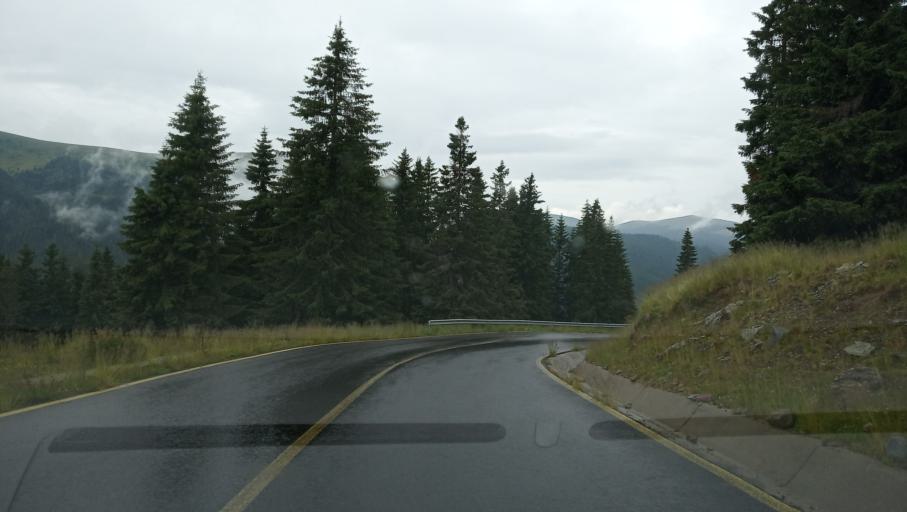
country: RO
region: Gorj
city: Novaci-Straini
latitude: 45.3897
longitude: 23.6401
